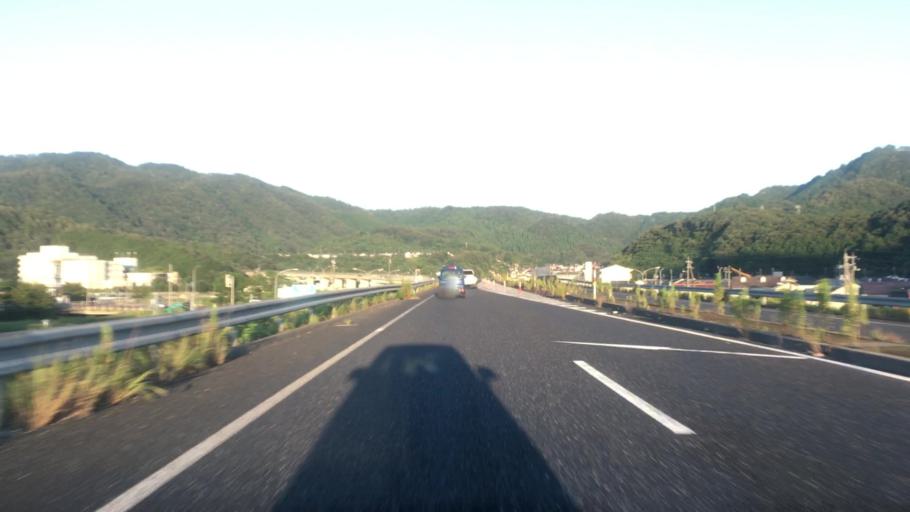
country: JP
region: Tottori
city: Tottori
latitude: 35.5236
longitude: 134.2270
